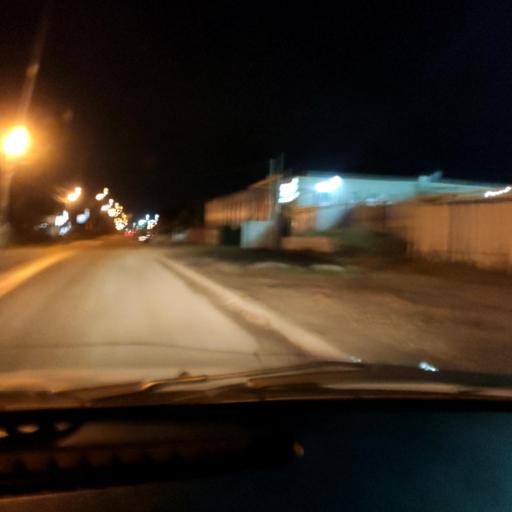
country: RU
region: Bashkortostan
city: Avdon
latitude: 54.6917
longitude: 55.7981
